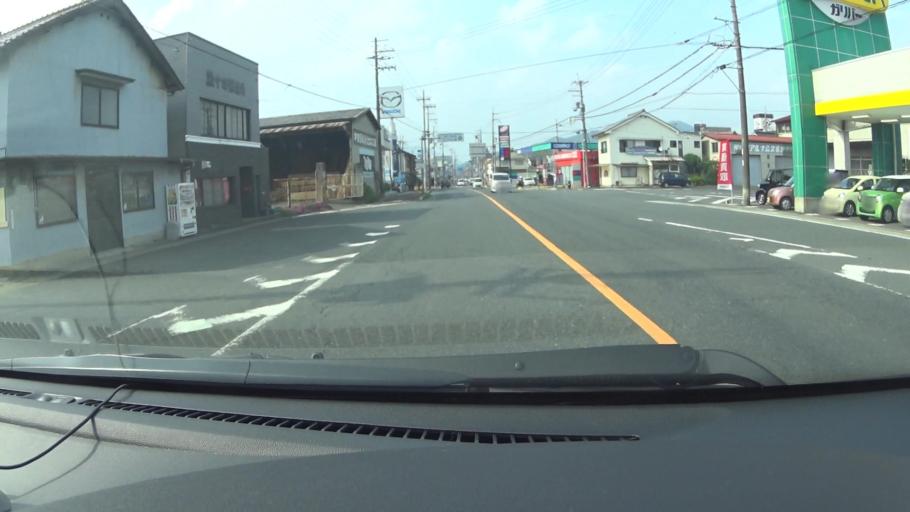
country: JP
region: Kyoto
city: Maizuru
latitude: 35.4355
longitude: 135.3284
